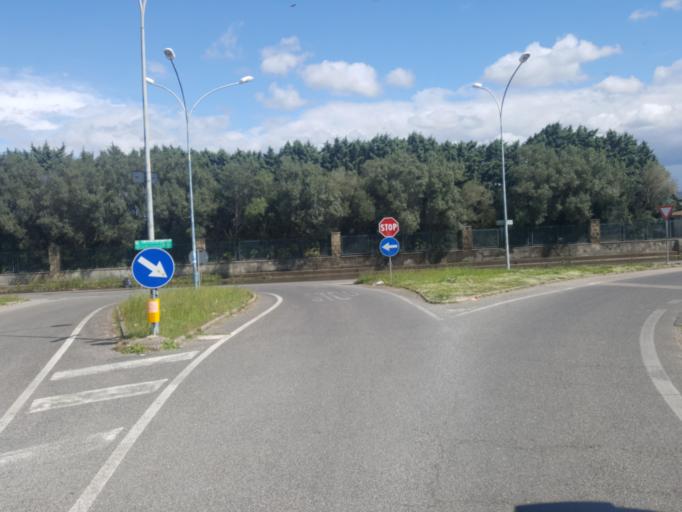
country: IT
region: Campania
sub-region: Provincia di Napoli
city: Masseria Vecchia Ovest
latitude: 40.9314
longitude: 14.0792
